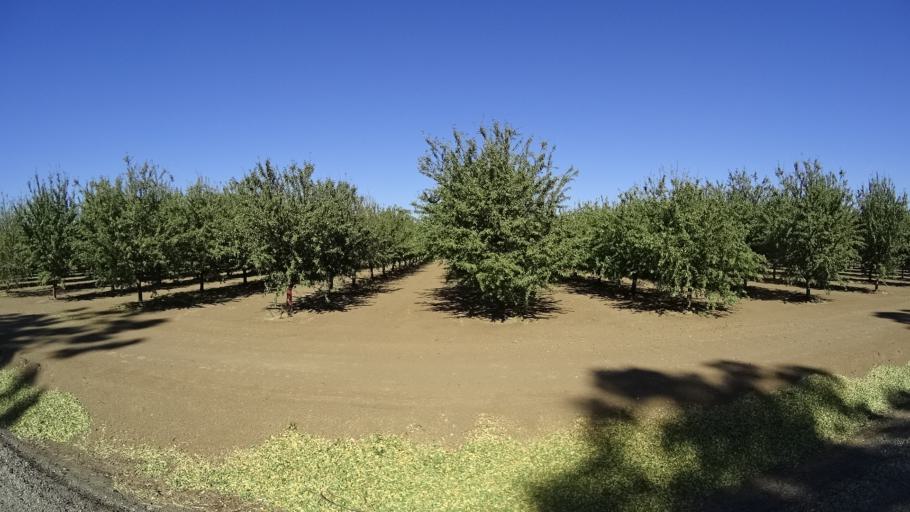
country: US
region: California
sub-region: Yolo County
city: Cottonwood
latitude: 38.6198
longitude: -121.8748
